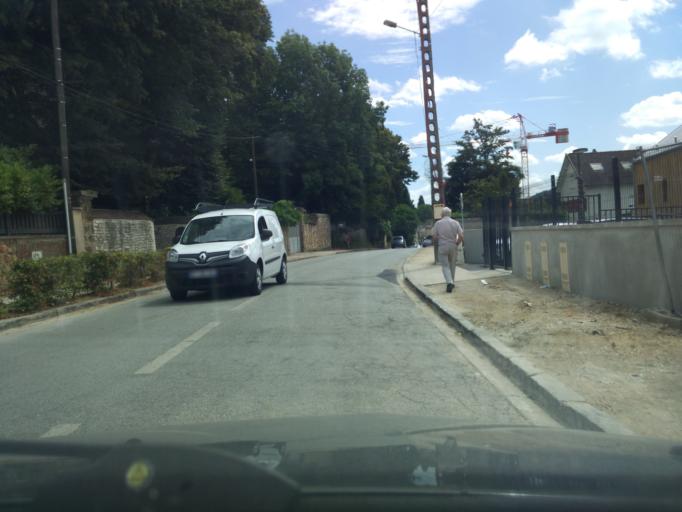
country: FR
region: Ile-de-France
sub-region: Departement des Yvelines
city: Saint-Remy-les-Chevreuse
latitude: 48.7047
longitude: 2.0980
